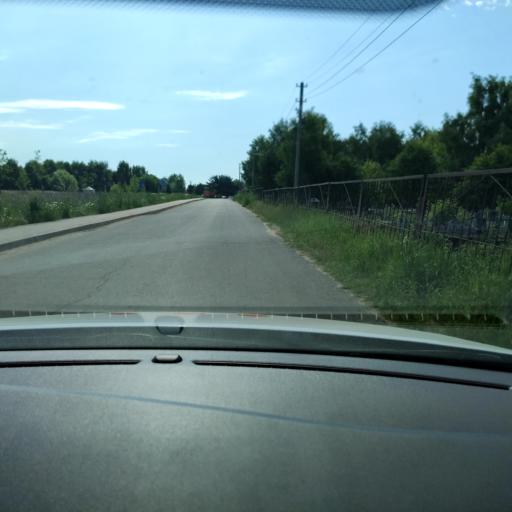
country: RU
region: Tatarstan
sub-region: Gorod Kazan'
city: Kazan
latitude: 55.8902
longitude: 49.0949
